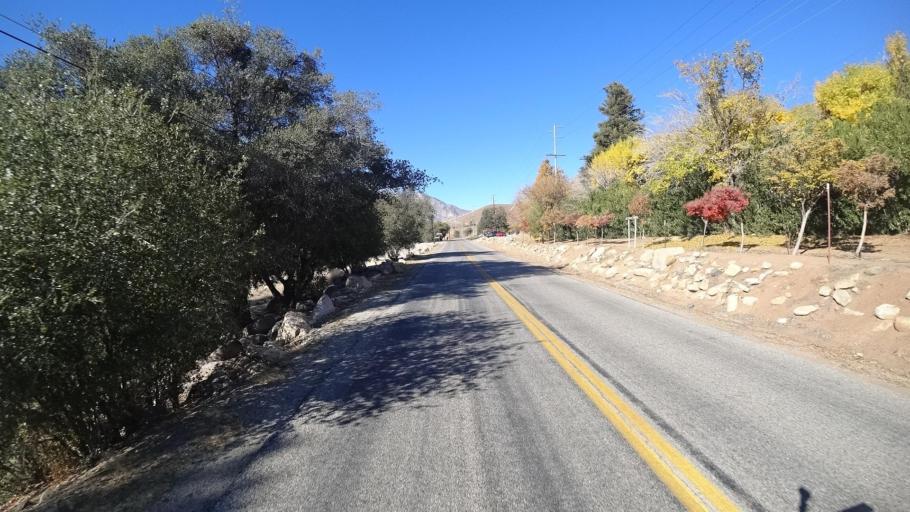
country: US
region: California
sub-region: Kern County
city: Kernville
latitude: 35.7683
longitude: -118.4289
